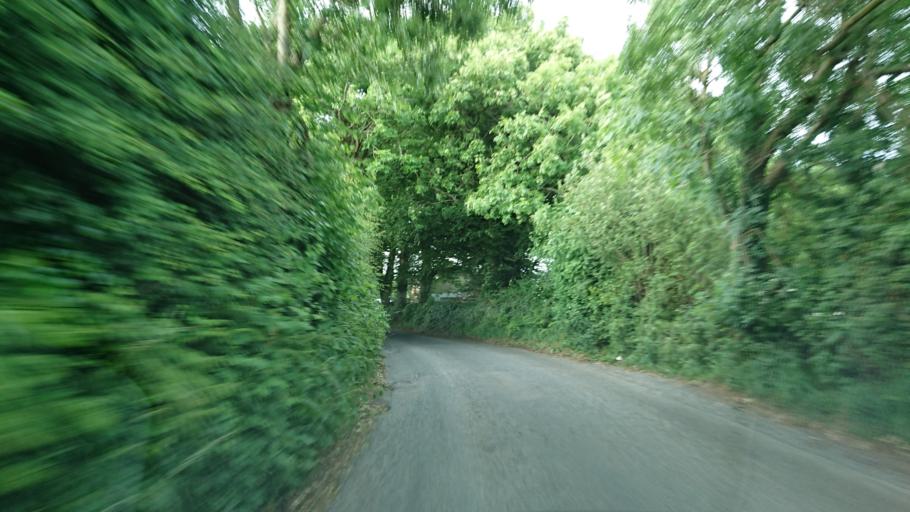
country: IE
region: Munster
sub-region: Waterford
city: Tra Mhor
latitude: 52.2160
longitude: -7.1866
